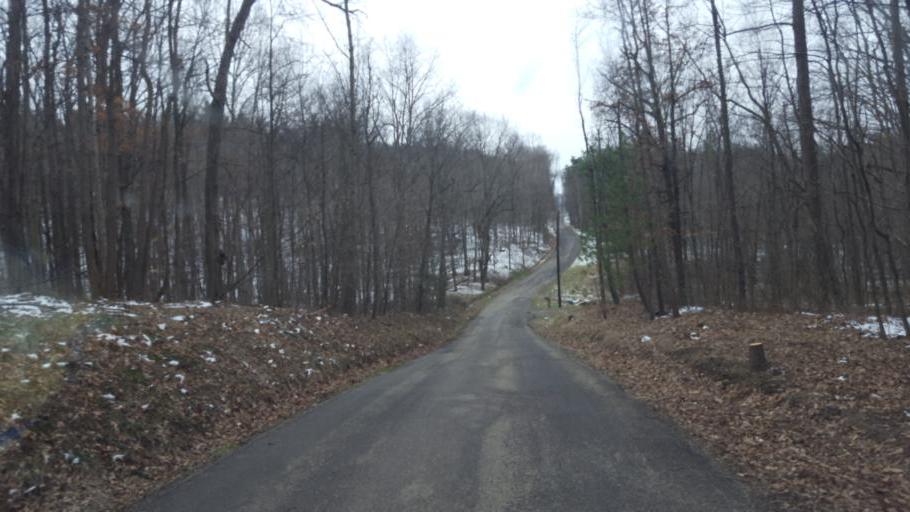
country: US
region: Ohio
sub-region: Sandusky County
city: Bellville
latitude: 40.5660
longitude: -82.4111
